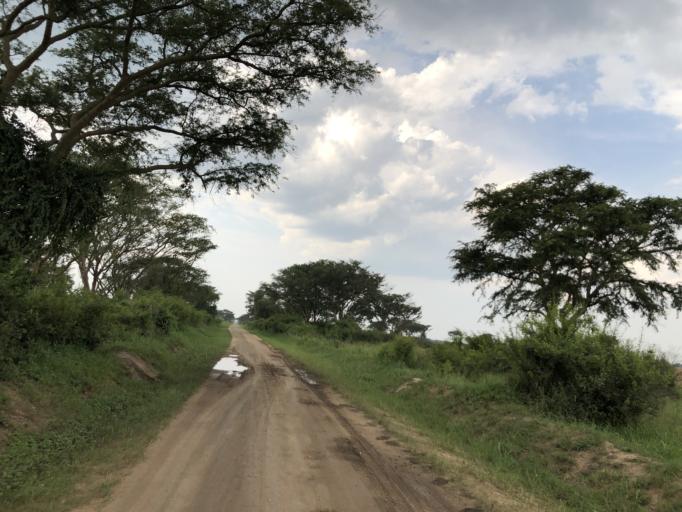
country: UG
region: Western Region
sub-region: Rubirizi District
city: Rubirizi
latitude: -0.1978
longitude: 30.0049
